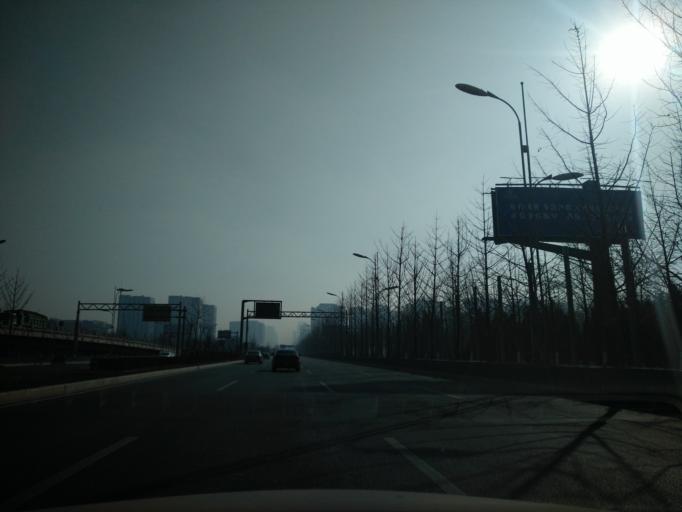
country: CN
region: Beijing
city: Jiugong
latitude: 39.8132
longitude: 116.4862
